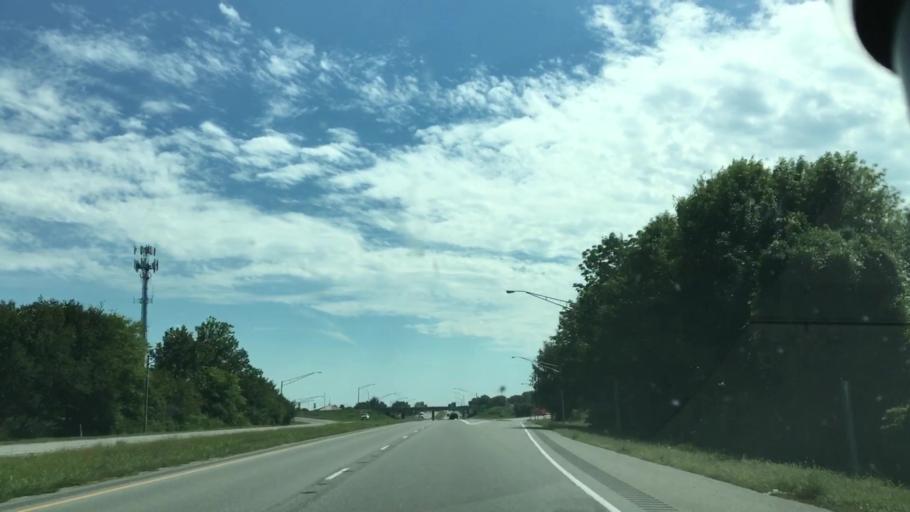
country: US
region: Kentucky
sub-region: Daviess County
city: Owensboro
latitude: 37.7594
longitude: -87.1609
